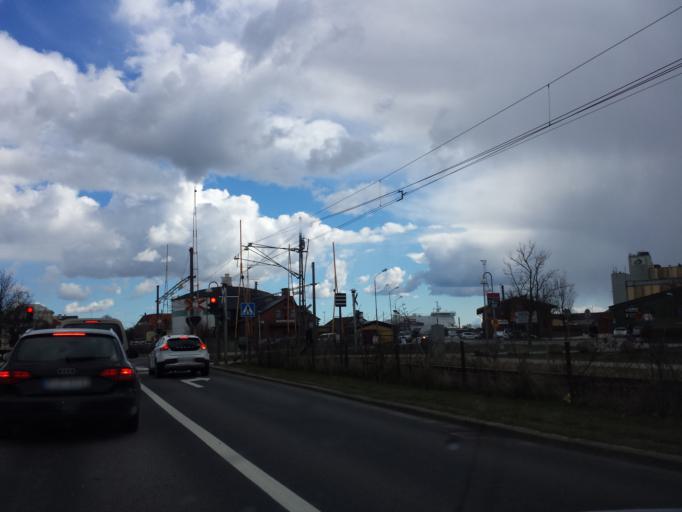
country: SE
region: Skane
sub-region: Ystads Kommun
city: Ystad
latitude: 55.4274
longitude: 13.8166
